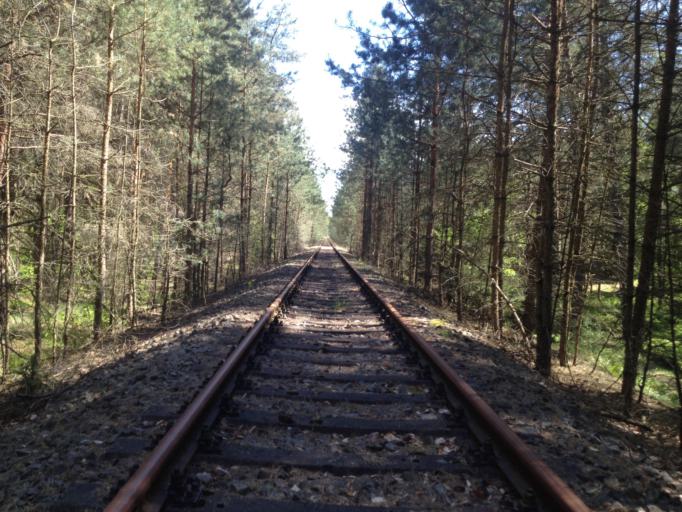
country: DE
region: Brandenburg
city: Lychen
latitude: 53.1711
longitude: 13.3593
